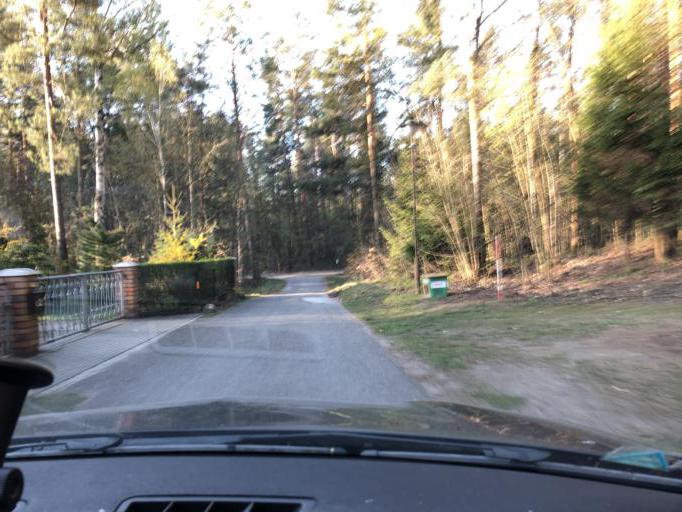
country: DE
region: Saxony
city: Krauschwitz
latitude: 51.5137
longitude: 14.7094
